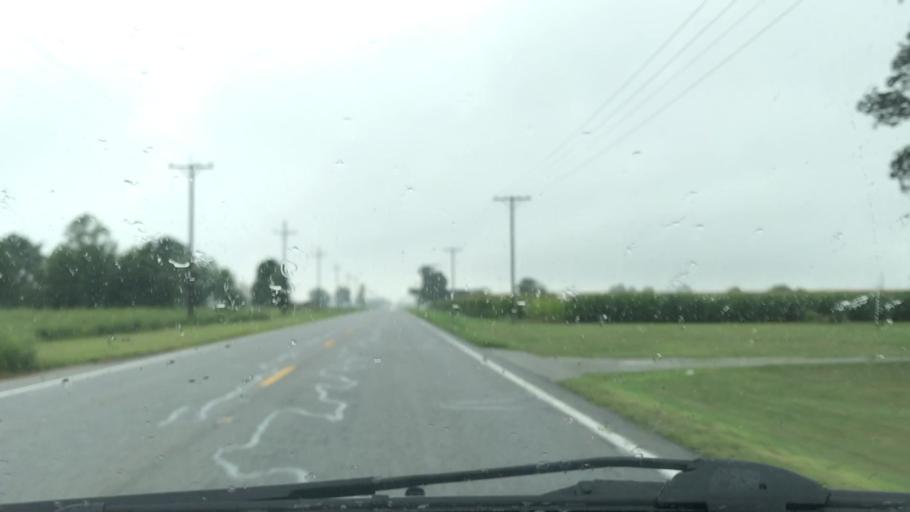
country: US
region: Indiana
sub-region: Hamilton County
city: Sheridan
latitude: 40.1284
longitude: -86.3074
